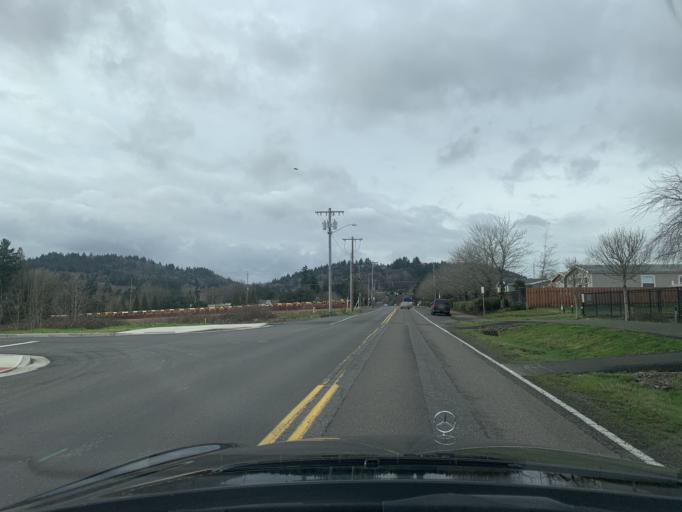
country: US
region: Oregon
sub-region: Multnomah County
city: Gresham
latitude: 45.4869
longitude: -122.4105
